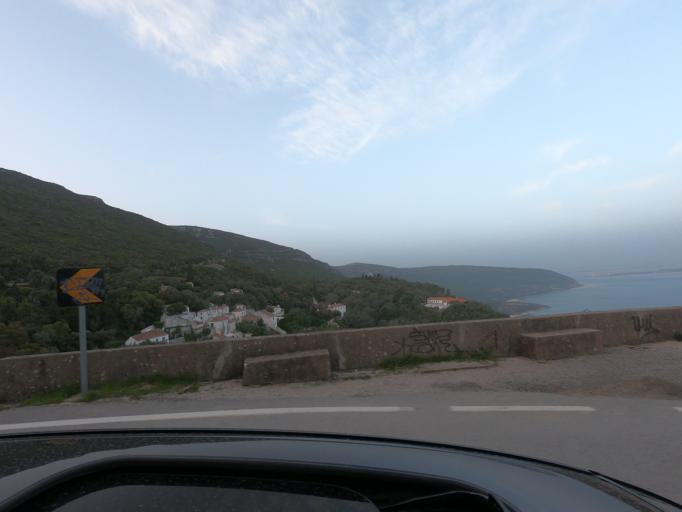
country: PT
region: Setubal
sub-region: Sesimbra
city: Sesimbra
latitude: 38.4724
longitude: -8.9959
